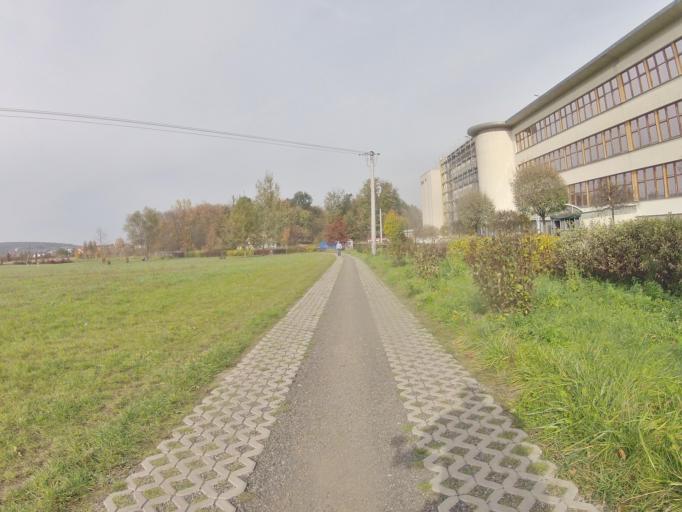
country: PL
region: Lesser Poland Voivodeship
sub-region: Krakow
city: Sidzina
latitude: 50.0261
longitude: 19.8997
